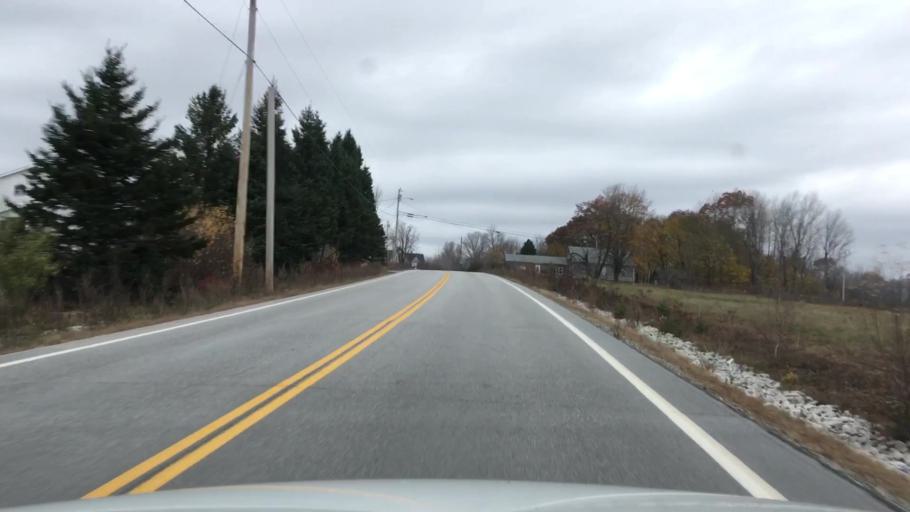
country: US
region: Maine
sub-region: Hancock County
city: Penobscot
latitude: 44.5195
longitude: -68.6593
